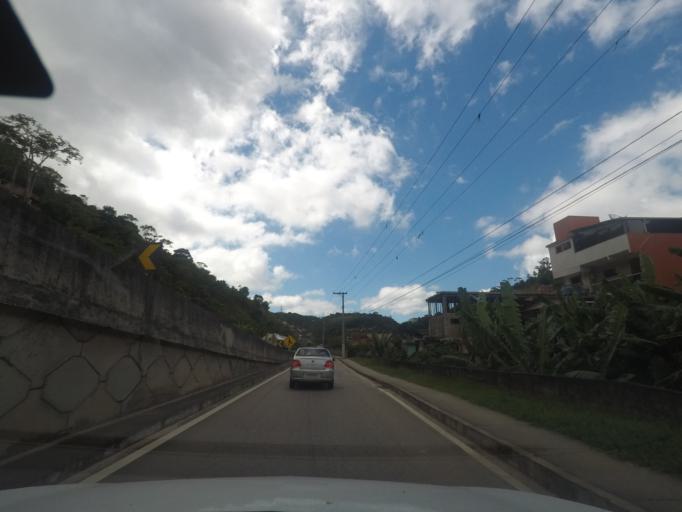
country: BR
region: Rio de Janeiro
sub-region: Teresopolis
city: Teresopolis
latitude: -22.3902
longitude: -42.9535
